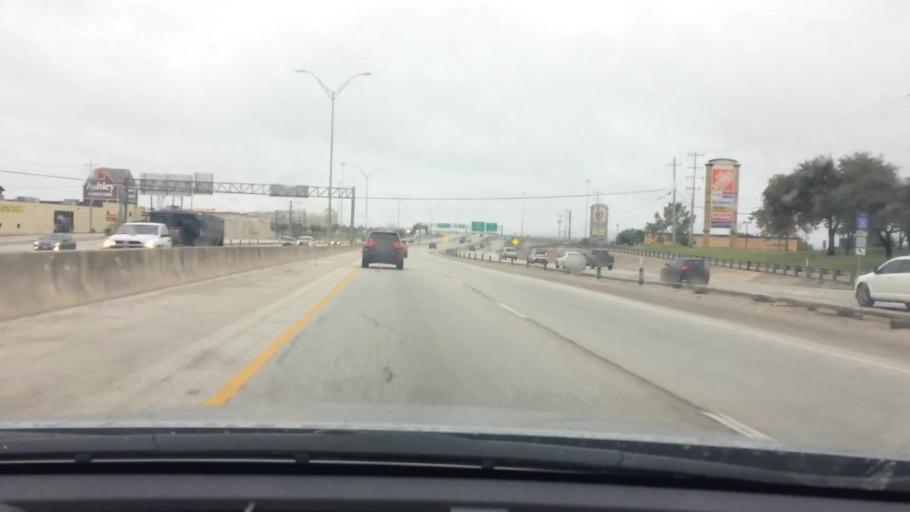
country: US
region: Texas
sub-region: Bexar County
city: Live Oak
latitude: 29.5633
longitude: -98.3292
